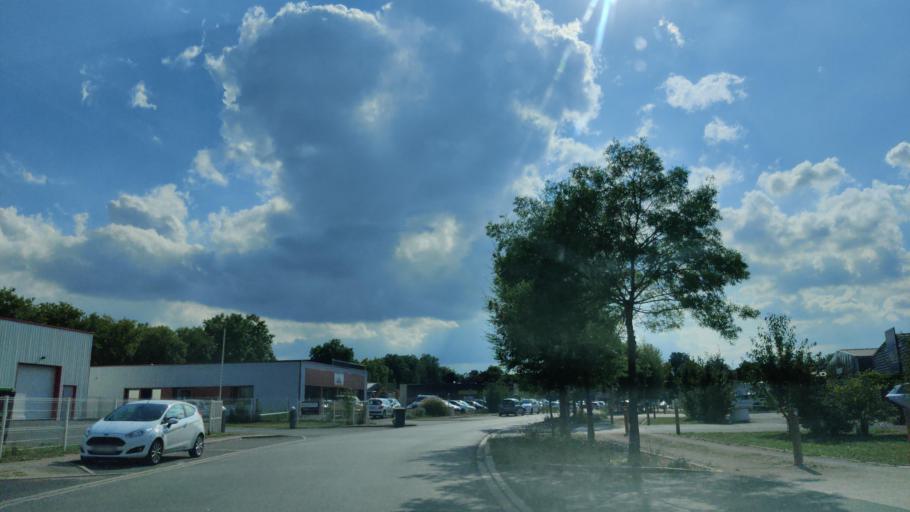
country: FR
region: Poitou-Charentes
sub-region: Departement des Deux-Sevres
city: Bessines
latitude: 46.3022
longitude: -0.4943
